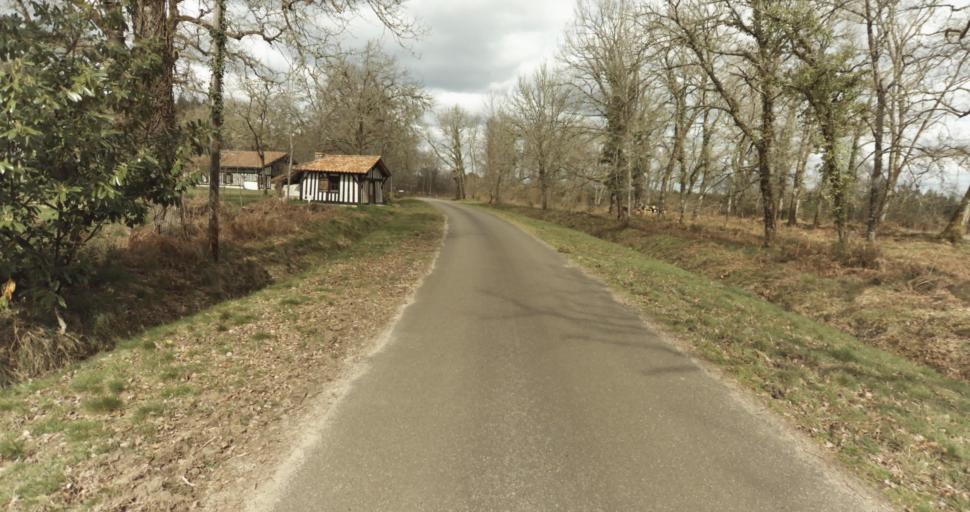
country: FR
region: Aquitaine
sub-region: Departement des Landes
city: Roquefort
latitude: 44.0946
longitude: -0.4539
